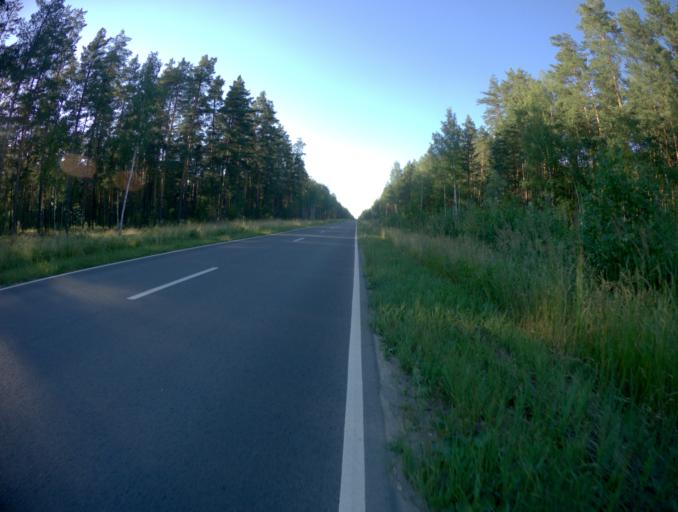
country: RU
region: Vladimir
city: Galitsy
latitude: 56.0643
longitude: 42.8662
